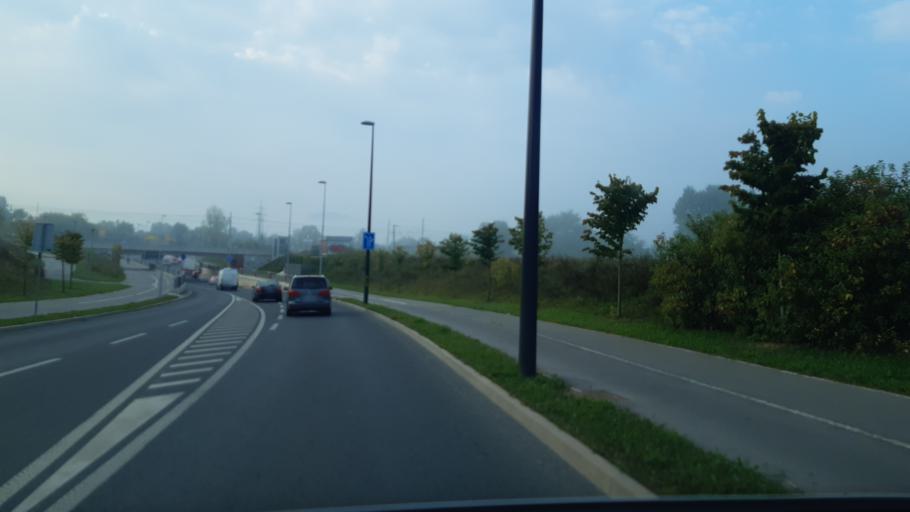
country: SI
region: Ljubljana
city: Ljubljana
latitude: 46.0393
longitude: 14.4650
